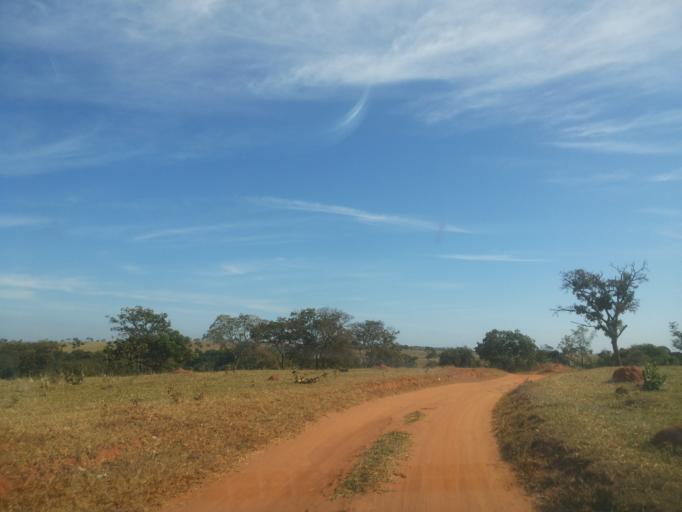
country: BR
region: Minas Gerais
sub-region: Ituiutaba
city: Ituiutaba
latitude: -19.1133
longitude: -49.4114
